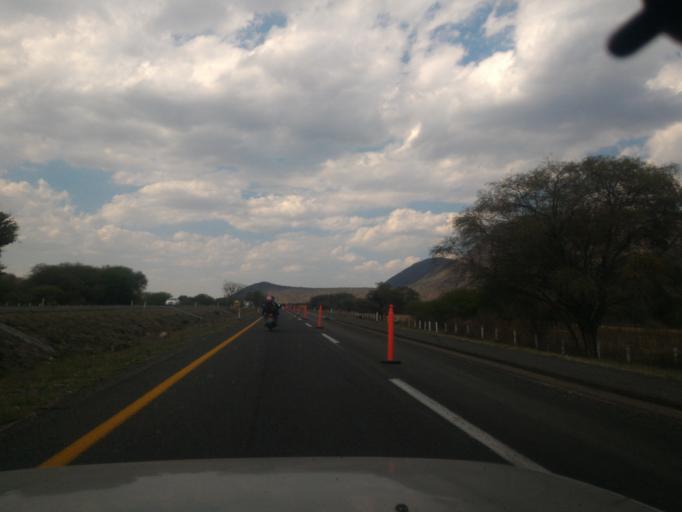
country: MX
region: Jalisco
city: Zacoalco de Torres
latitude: 20.1747
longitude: -103.5084
